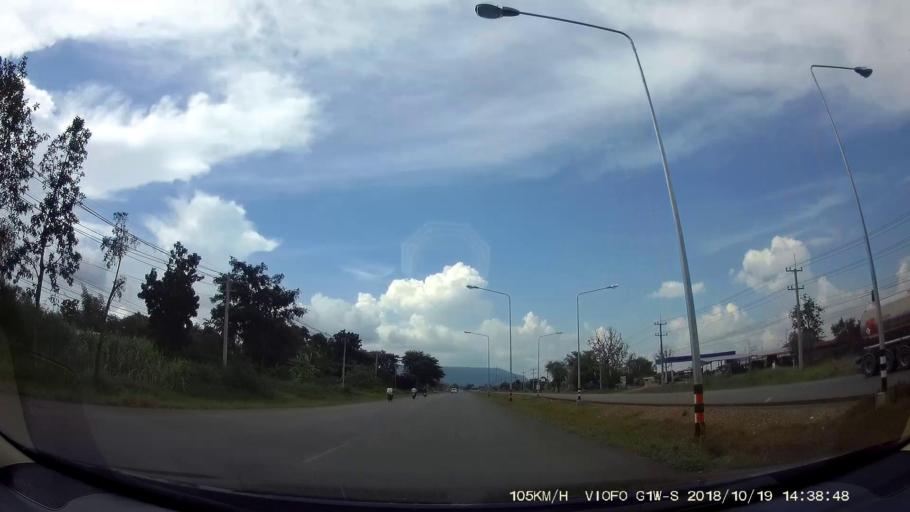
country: TH
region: Chaiyaphum
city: Kaeng Khro
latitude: 16.2180
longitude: 102.1990
